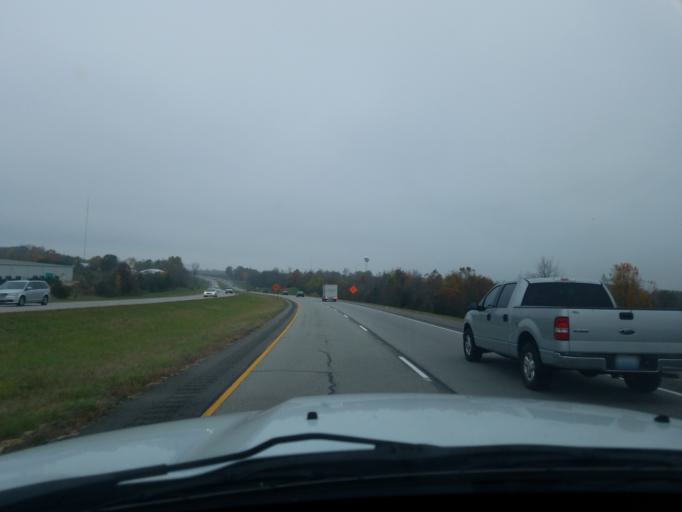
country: US
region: Kentucky
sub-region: Hardin County
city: Elizabethtown
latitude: 37.6583
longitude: -85.8363
